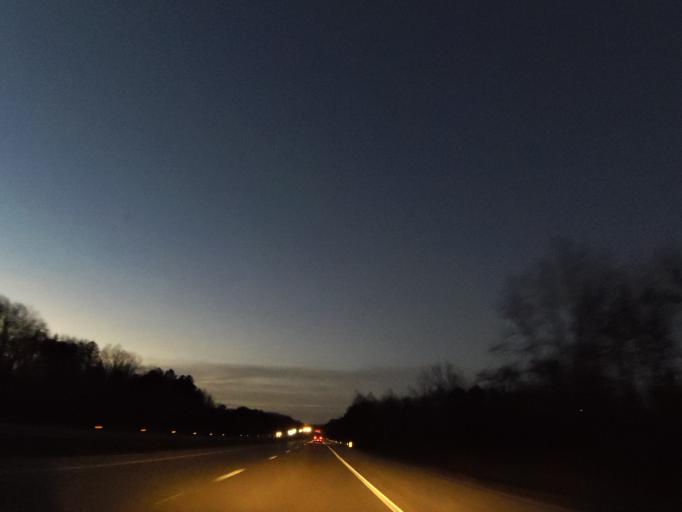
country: US
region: Kentucky
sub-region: Laurel County
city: London
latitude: 37.1926
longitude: -84.1474
